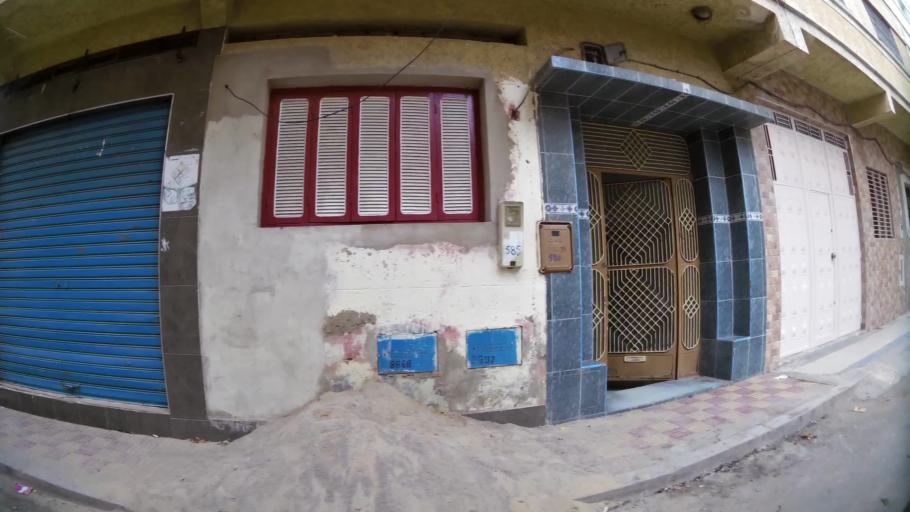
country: MA
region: Oriental
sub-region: Nador
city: Nador
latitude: 35.1648
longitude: -2.9314
